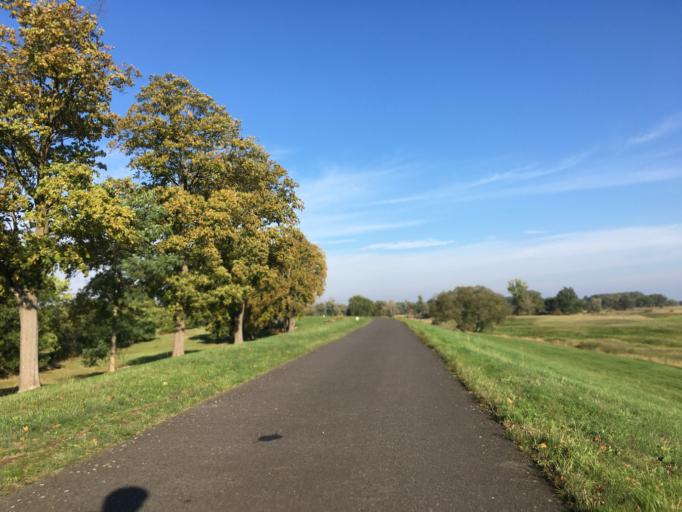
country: DE
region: Brandenburg
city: Reitwein
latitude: 52.5086
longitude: 14.6046
